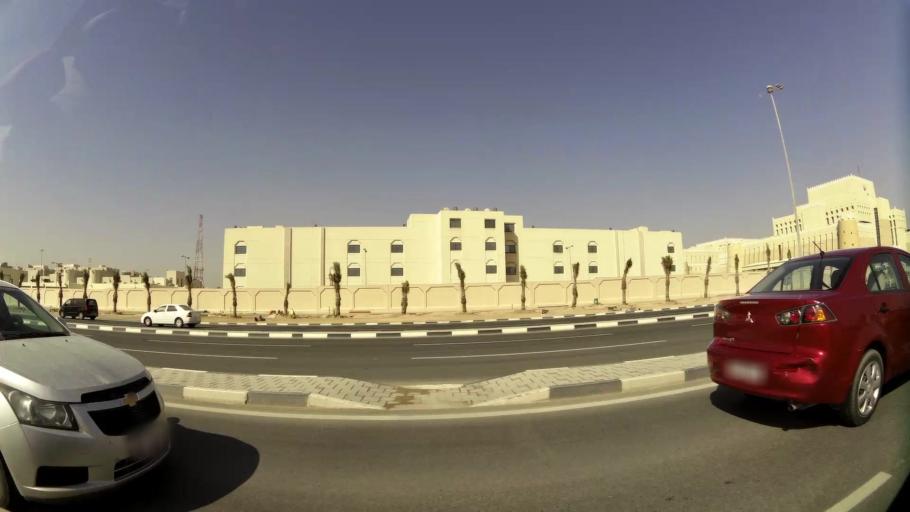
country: QA
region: Baladiyat ad Dawhah
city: Doha
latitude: 25.3038
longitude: 51.5066
